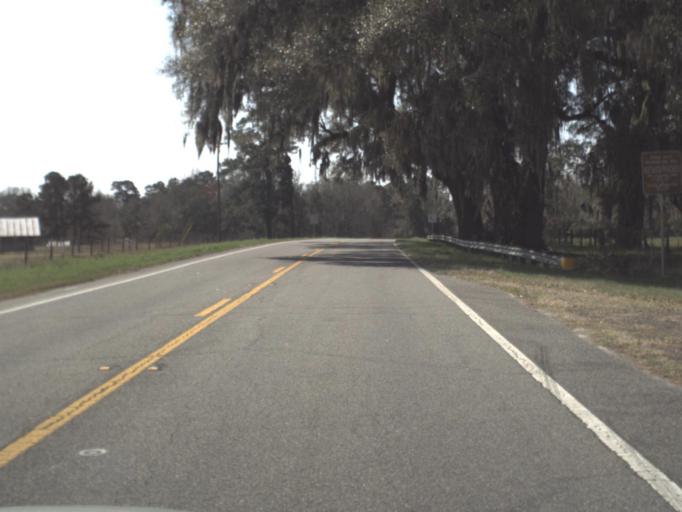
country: US
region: Florida
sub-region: Gadsden County
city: Havana
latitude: 30.5942
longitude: -84.4826
